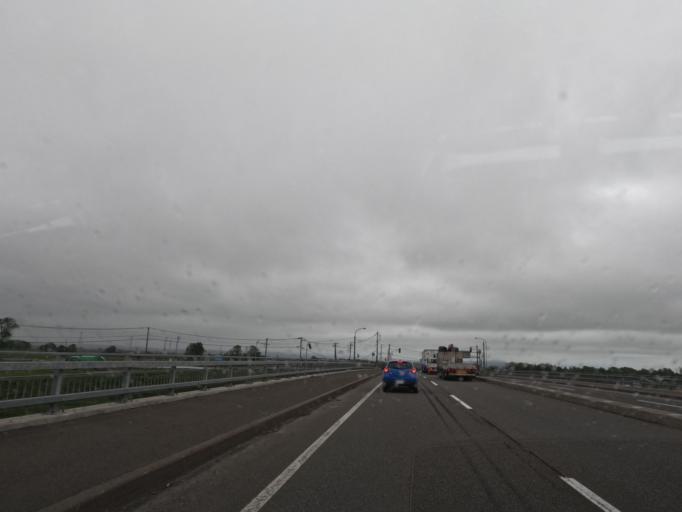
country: JP
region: Hokkaido
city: Tobetsu
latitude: 43.1629
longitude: 141.5198
